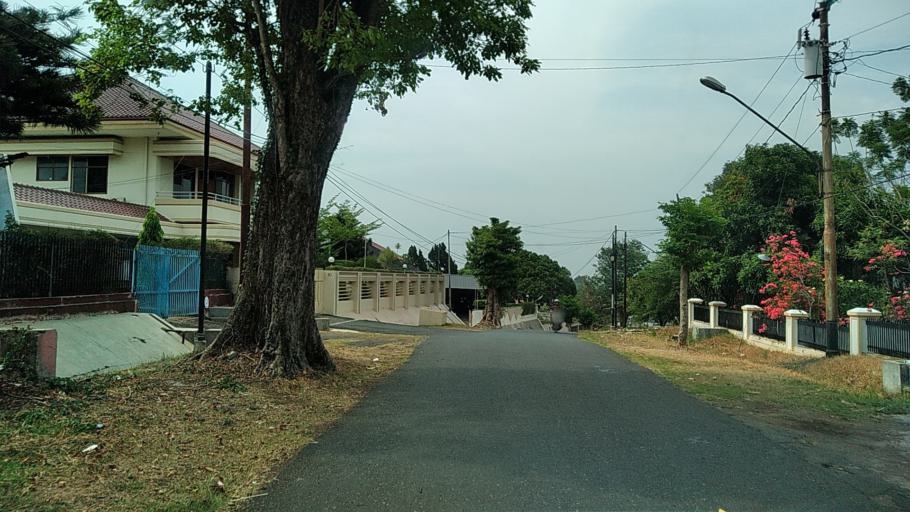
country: ID
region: Central Java
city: Semarang
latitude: -7.0056
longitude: 110.4205
